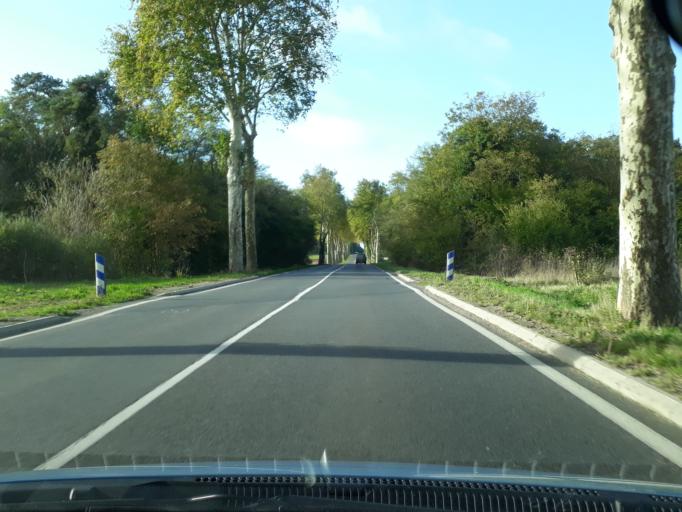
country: FR
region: Ile-de-France
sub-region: Departement de Seine-et-Marne
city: La Chapelle-la-Reine
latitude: 48.3265
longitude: 2.5837
